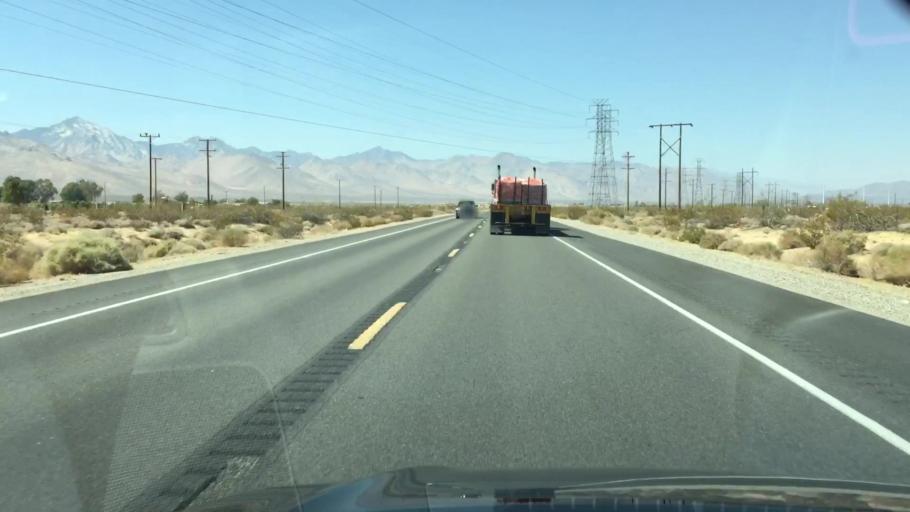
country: US
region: California
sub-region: Kern County
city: Inyokern
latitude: 35.6402
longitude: -117.7909
